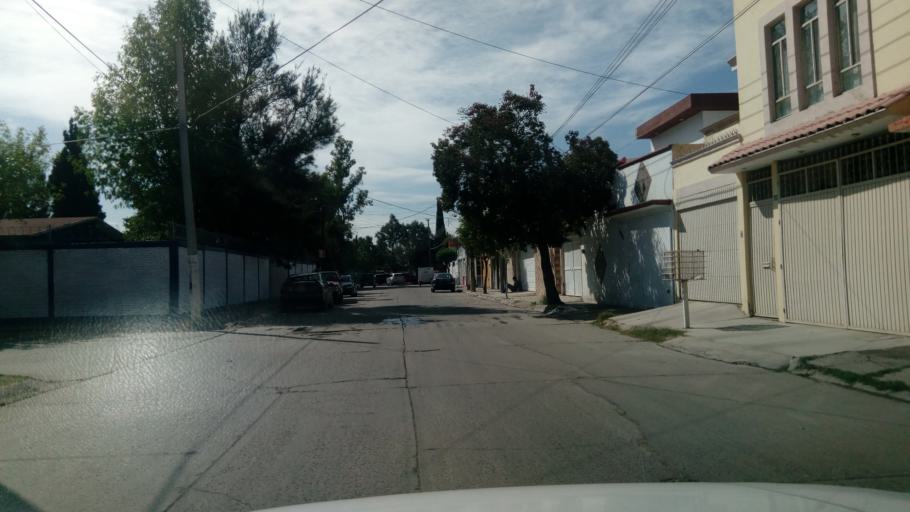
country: MX
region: Durango
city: Victoria de Durango
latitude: 24.0029
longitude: -104.6688
